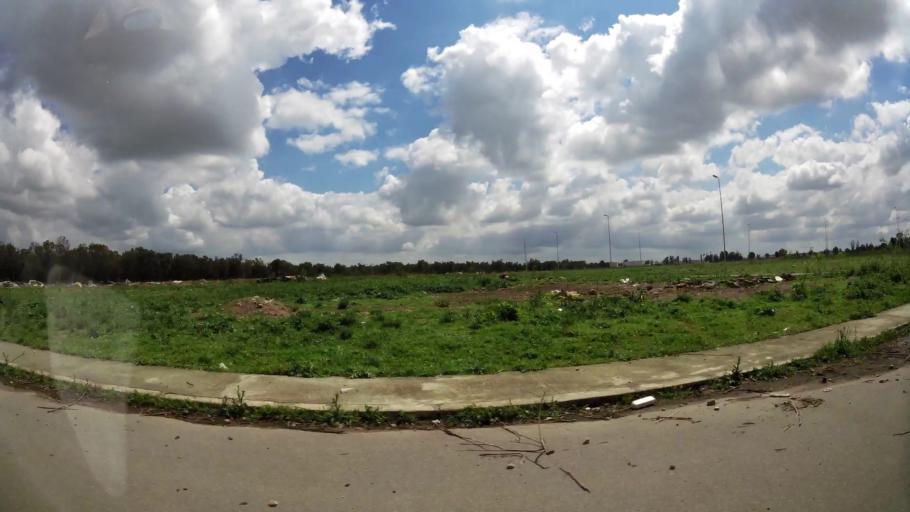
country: MA
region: Chaouia-Ouardigha
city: Nouaseur
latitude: 33.3846
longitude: -7.5578
